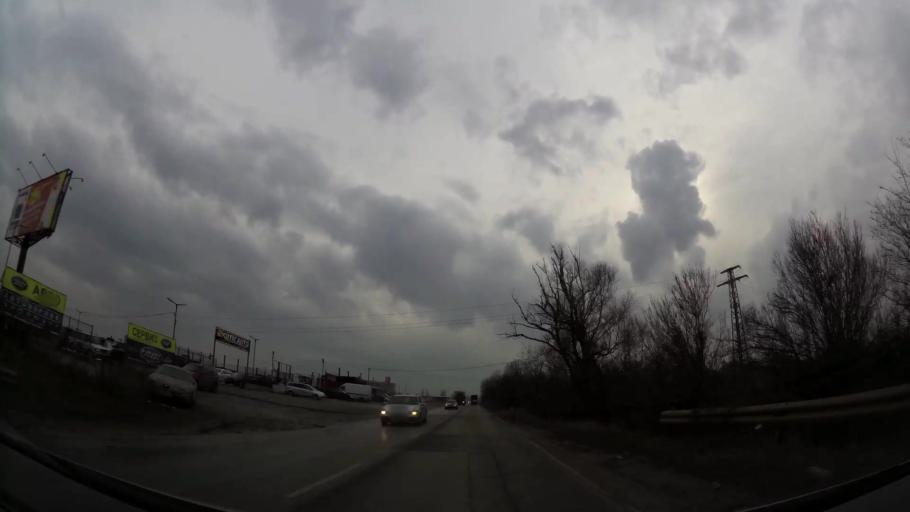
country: BG
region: Sofiya
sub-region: Obshtina Bozhurishte
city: Bozhurishte
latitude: 42.7004
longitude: 23.2303
